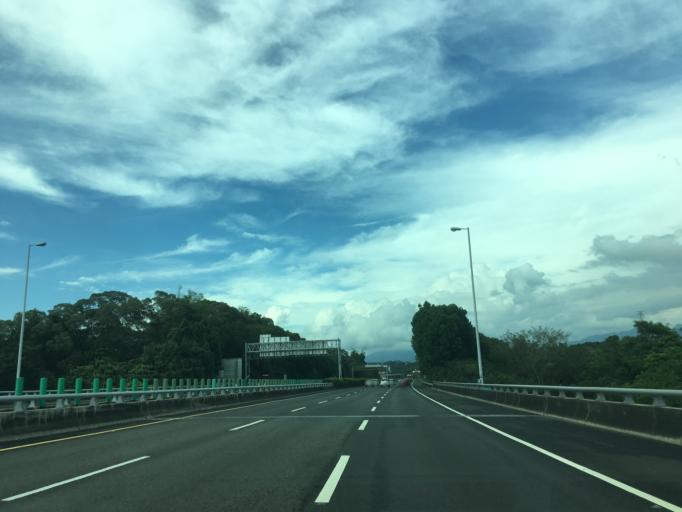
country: TW
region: Taiwan
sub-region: Chiayi
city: Jiayi Shi
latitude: 23.4562
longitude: 120.4890
